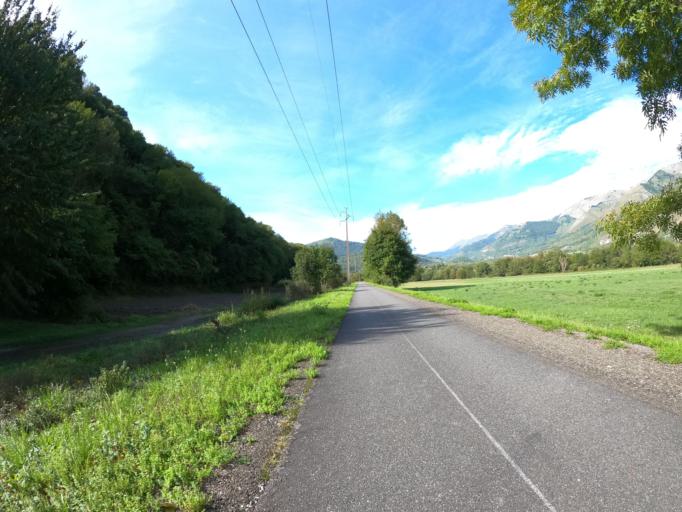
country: FR
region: Midi-Pyrenees
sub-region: Departement des Hautes-Pyrenees
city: Argeles-Gazost
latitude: 43.0234
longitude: -0.0758
